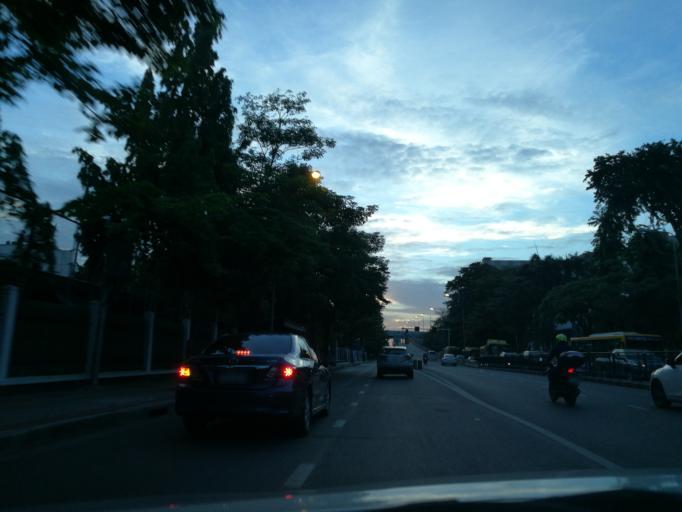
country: TH
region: Bangkok
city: Ratchathewi
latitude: 13.7678
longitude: 100.5324
